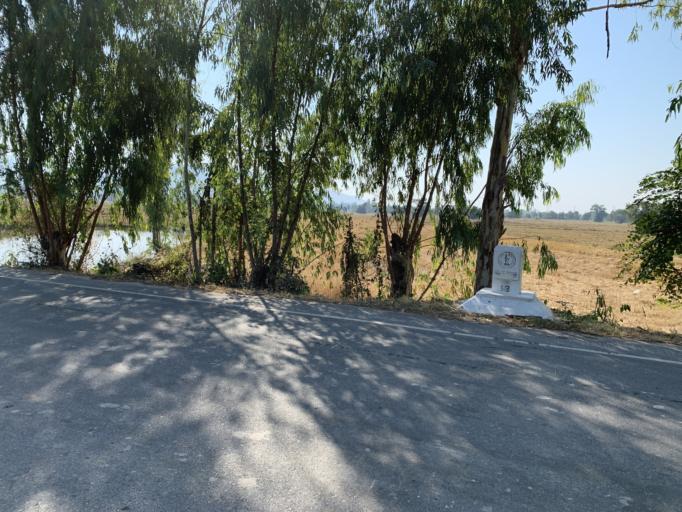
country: TH
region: Uttaradit
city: Phichai
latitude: 17.3553
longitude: 100.2118
